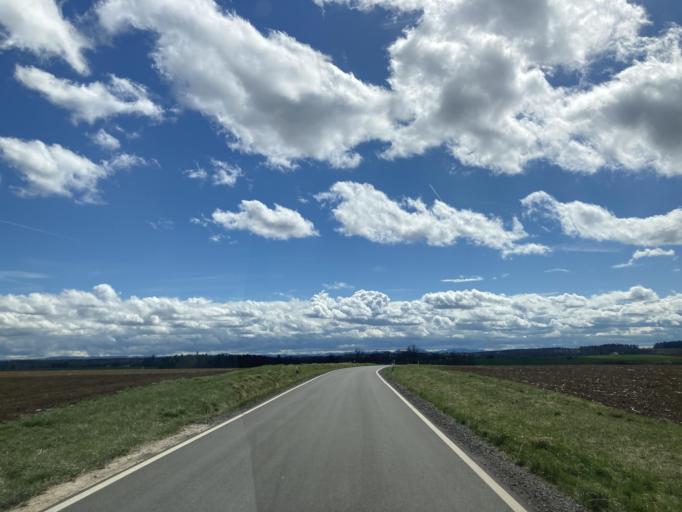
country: DE
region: Baden-Wuerttemberg
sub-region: Regierungsbezirk Stuttgart
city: Bondorf
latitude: 48.4636
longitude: 8.8104
